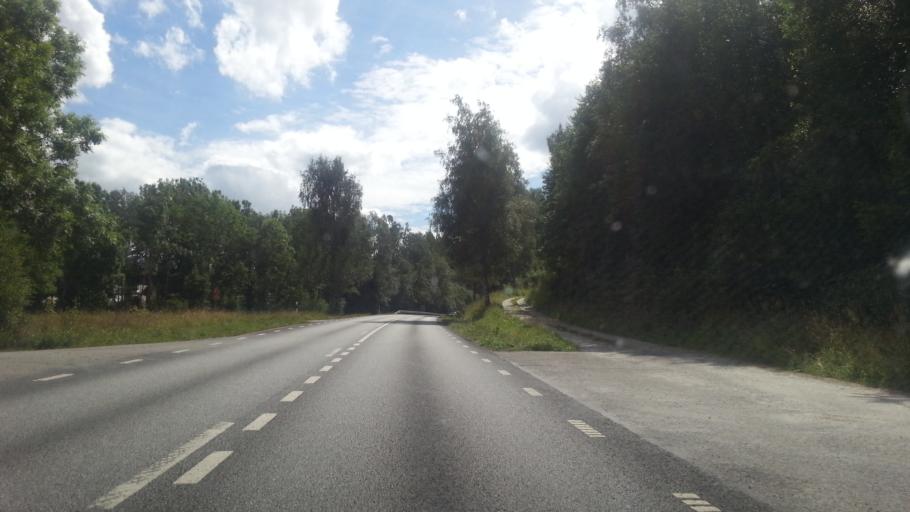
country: SE
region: OErebro
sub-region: Lindesbergs Kommun
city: Stora
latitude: 59.6591
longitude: 15.1034
